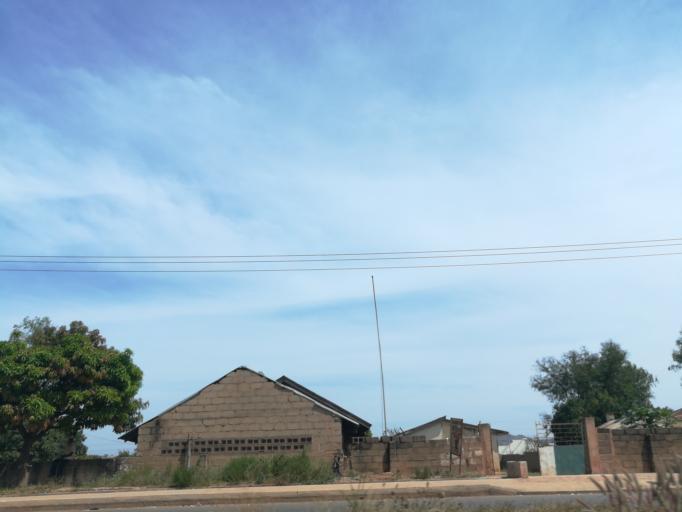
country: NG
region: Plateau
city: Bukuru
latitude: 9.7756
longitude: 8.8605
